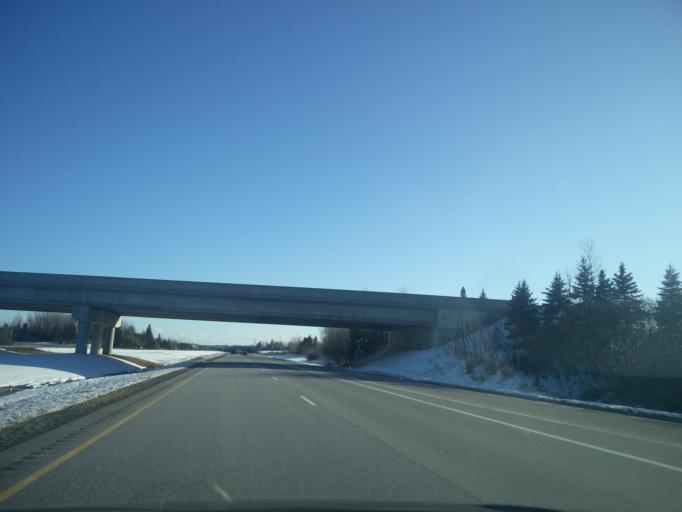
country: CA
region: Ontario
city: Prescott
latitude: 45.0300
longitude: -75.6259
